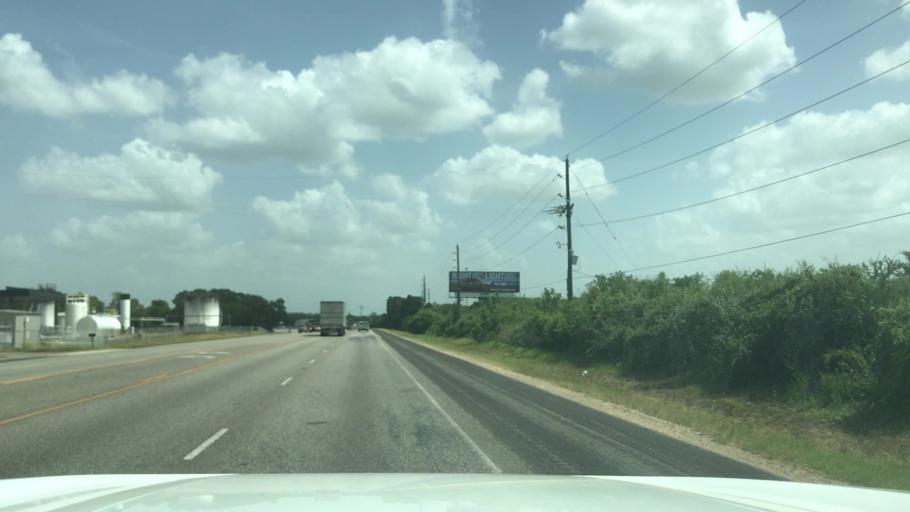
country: US
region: Texas
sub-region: Robertson County
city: Hearne
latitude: 30.8632
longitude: -96.5816
